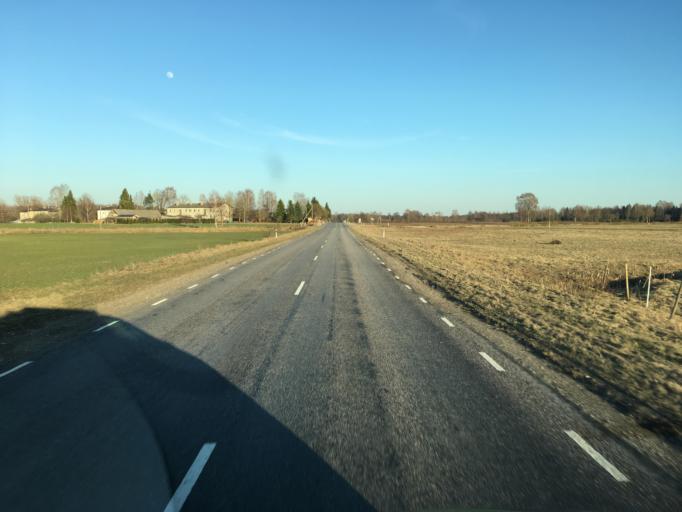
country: EE
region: Raplamaa
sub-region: Rapla vald
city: Rapla
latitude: 59.0835
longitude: 24.8213
